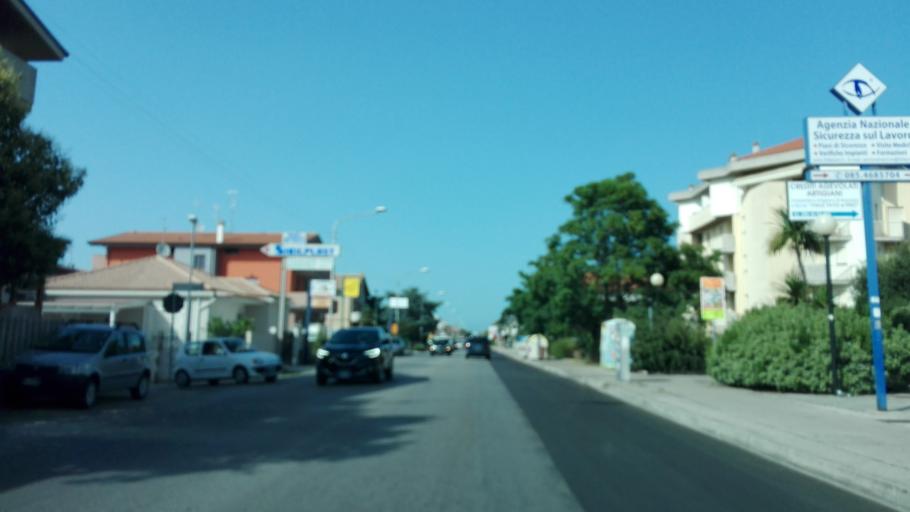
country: IT
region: Abruzzo
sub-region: Provincia di Pescara
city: Montesilvano Marina
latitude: 42.5052
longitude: 14.1378
